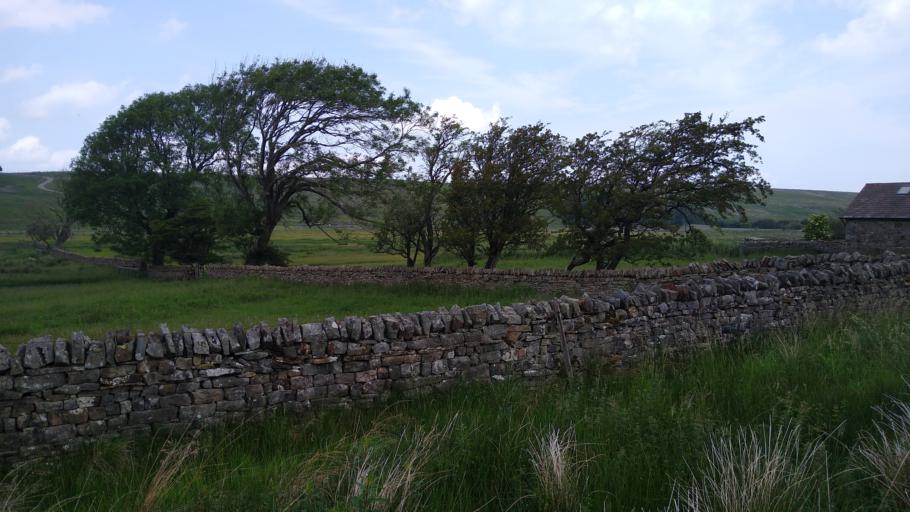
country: GB
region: England
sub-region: Cumbria
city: Brampton
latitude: 54.9170
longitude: -2.6269
